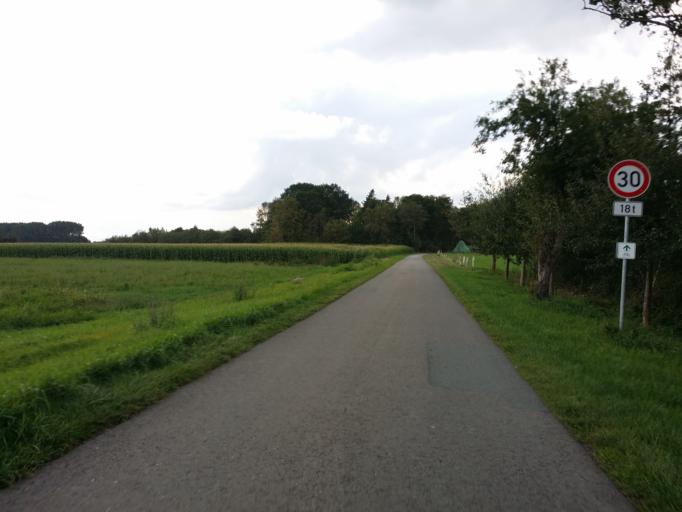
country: DE
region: Lower Saxony
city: Hemmoor
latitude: 53.6696
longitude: 9.1514
